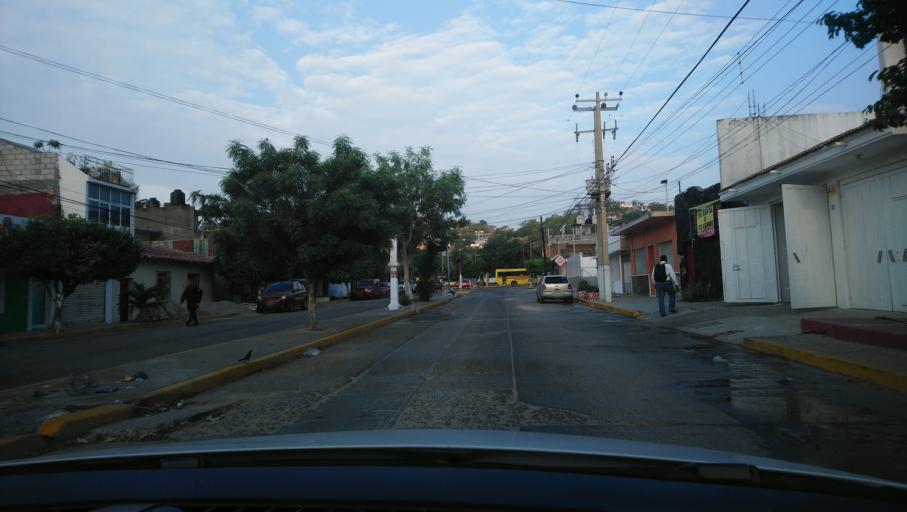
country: MX
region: Oaxaca
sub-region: Salina Cruz
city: Salina Cruz
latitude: 16.1836
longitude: -95.1984
